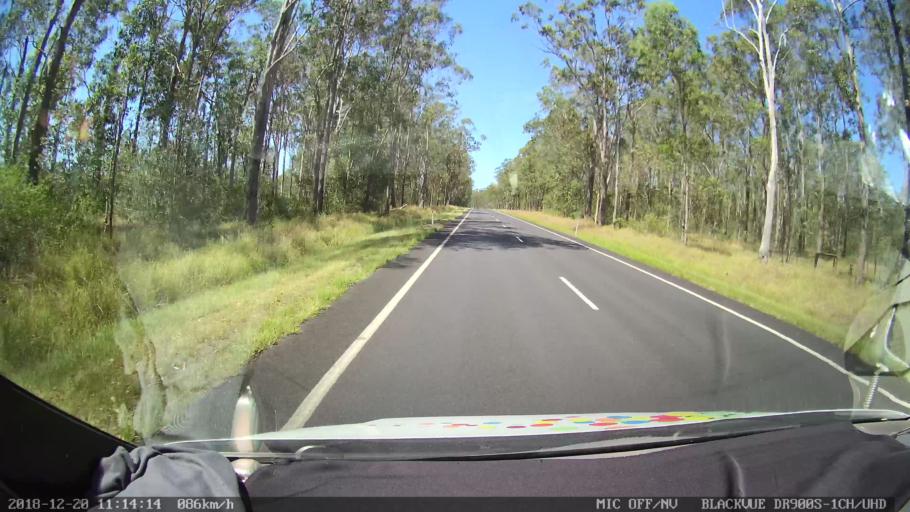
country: AU
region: New South Wales
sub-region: Richmond Valley
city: Casino
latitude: -28.9982
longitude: 153.0098
